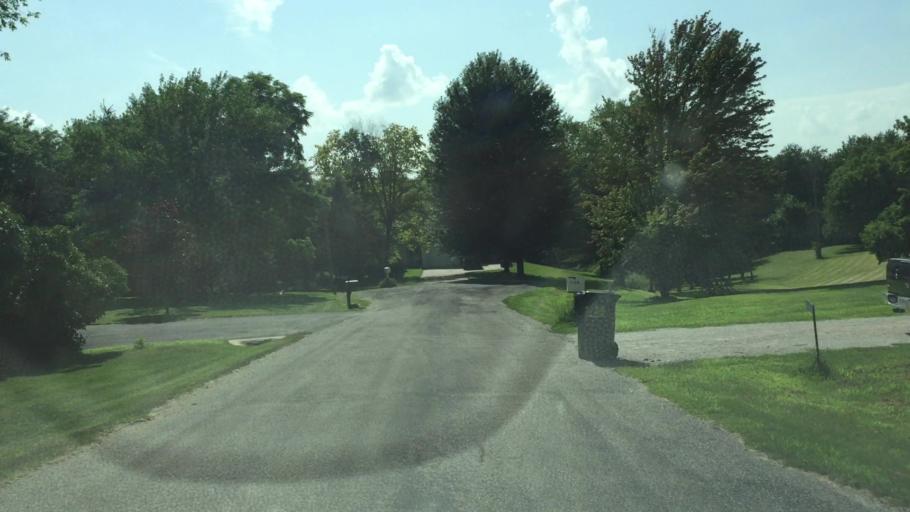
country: US
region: Iowa
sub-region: Johnson County
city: North Liberty
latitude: 41.8052
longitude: -91.6192
